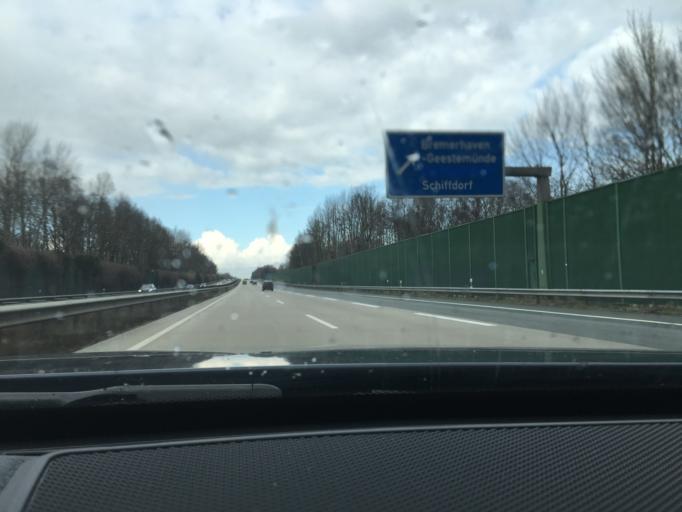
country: DE
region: Lower Saxony
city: Schiffdorf
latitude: 53.5206
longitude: 8.6262
